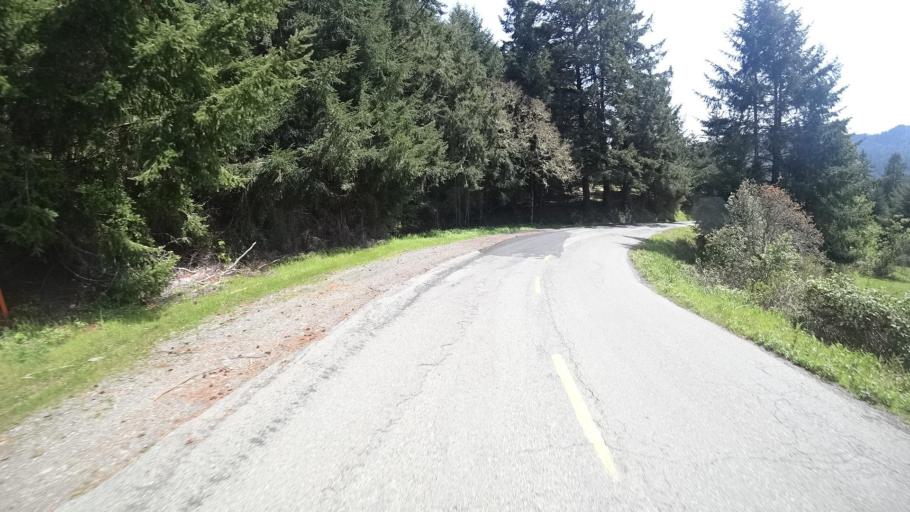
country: US
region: California
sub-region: Humboldt County
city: Redway
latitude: 40.3950
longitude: -123.7447
